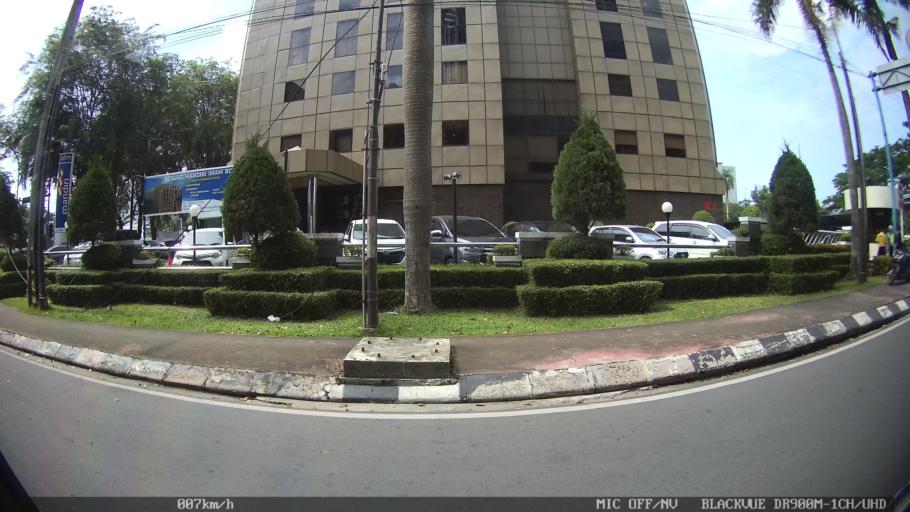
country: ID
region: North Sumatra
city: Medan
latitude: 3.5869
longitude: 98.6748
